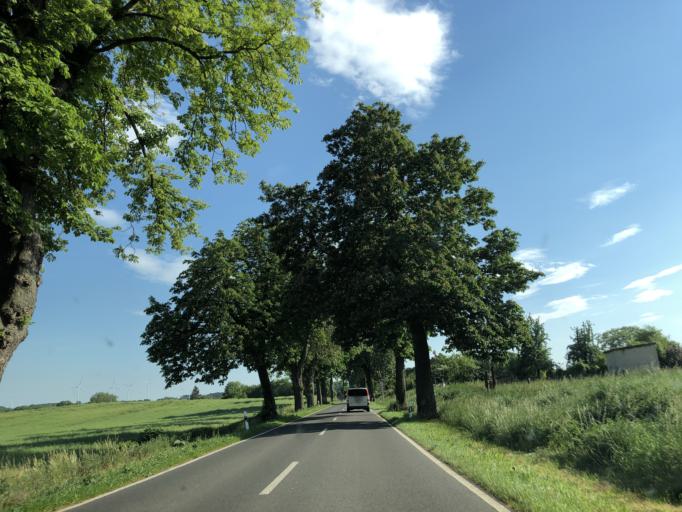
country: DE
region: Brandenburg
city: Angermunde
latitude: 53.1001
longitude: 13.9642
